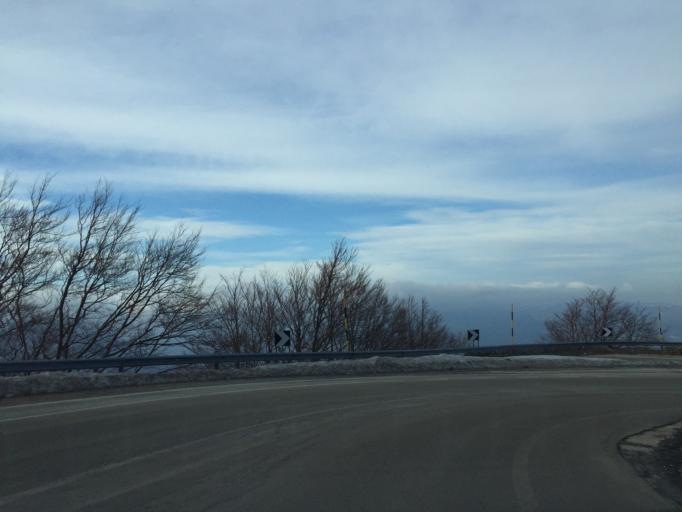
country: IT
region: Molise
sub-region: Provincia di Campobasso
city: San Massimo
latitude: 41.4698
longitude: 14.3948
